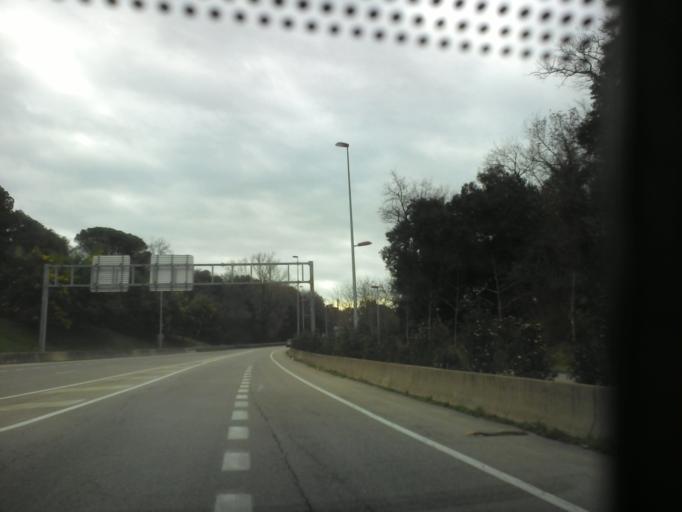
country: ES
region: Catalonia
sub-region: Provincia de Girona
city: Fornells de la Selva
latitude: 41.9549
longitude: 2.8120
